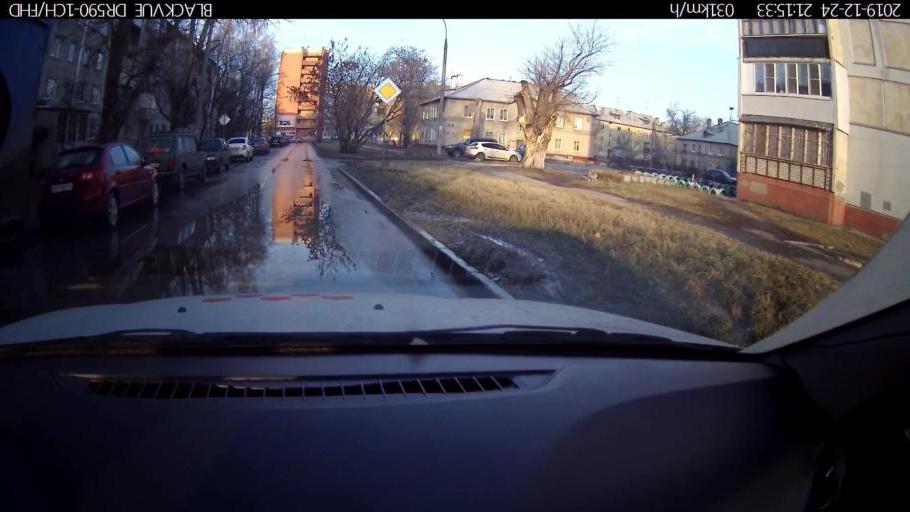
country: RU
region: Nizjnij Novgorod
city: Nizhniy Novgorod
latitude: 56.2662
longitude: 43.8838
